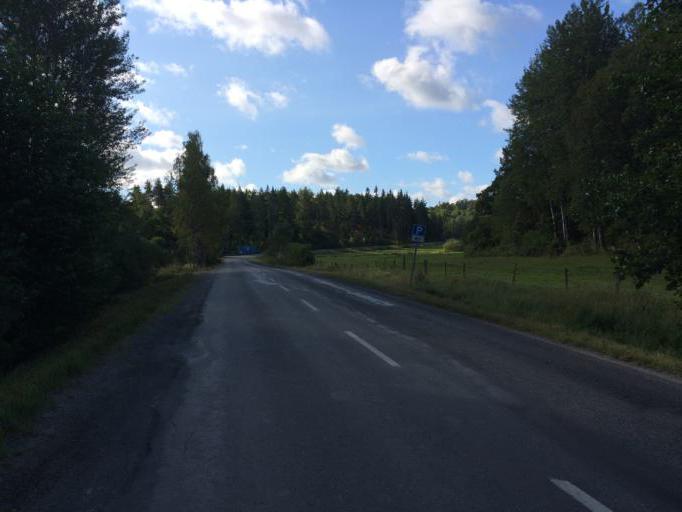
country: SE
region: Stockholm
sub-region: Haninge Kommun
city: Handen
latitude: 59.2187
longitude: 18.0818
